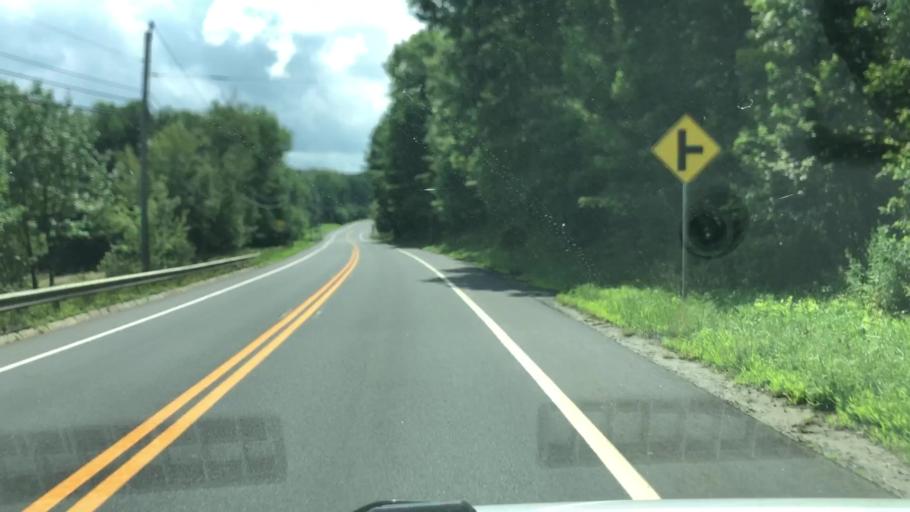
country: US
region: Massachusetts
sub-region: Franklin County
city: Ashfield
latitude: 42.5124
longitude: -72.8091
